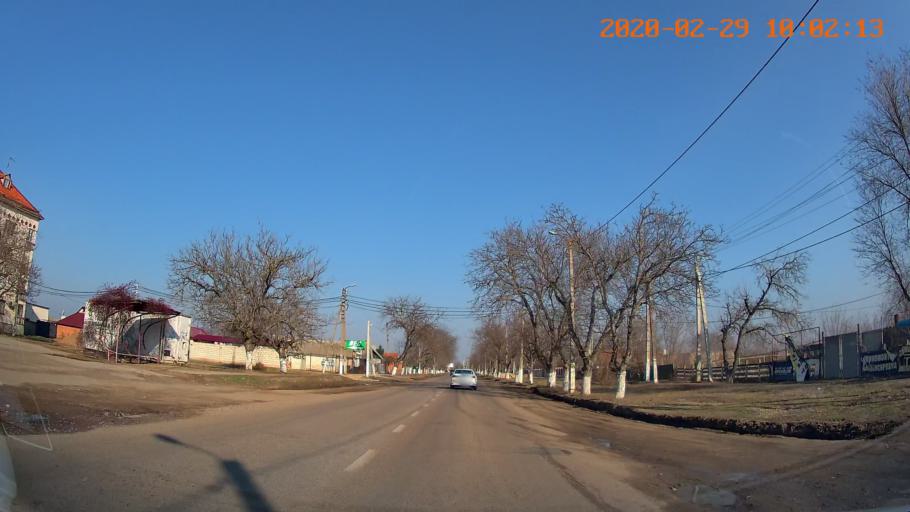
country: MD
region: Telenesti
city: Slobozia
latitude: 46.7812
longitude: 29.6838
